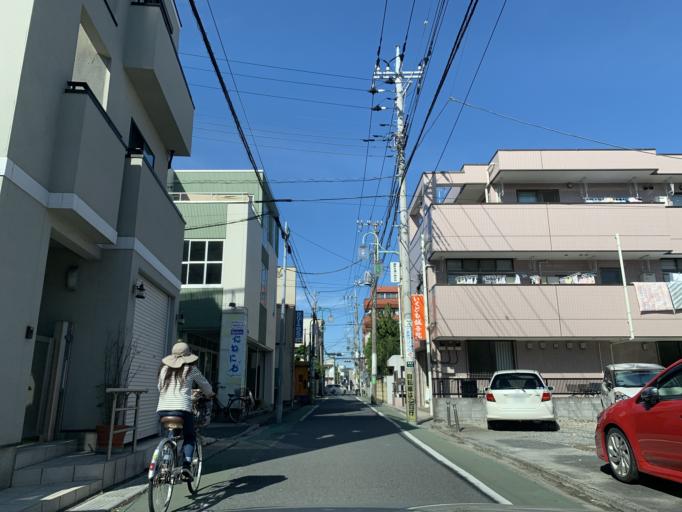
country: JP
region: Chiba
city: Matsudo
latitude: 35.7267
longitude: 139.9273
